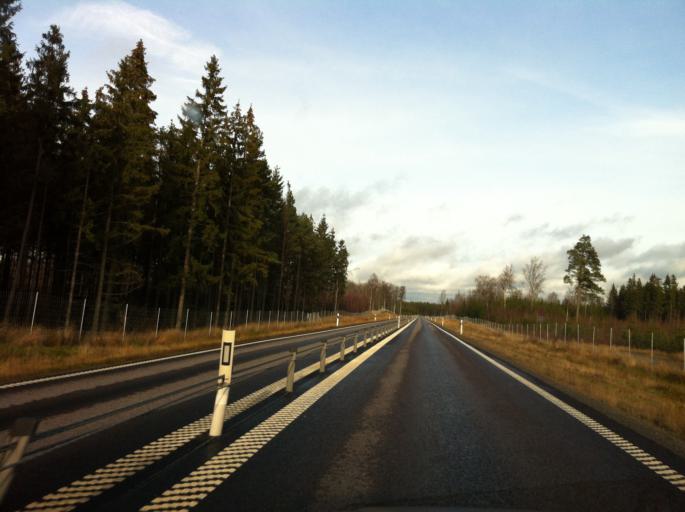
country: SE
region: Kronoberg
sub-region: Almhults Kommun
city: AElmhult
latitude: 56.6379
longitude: 14.2644
